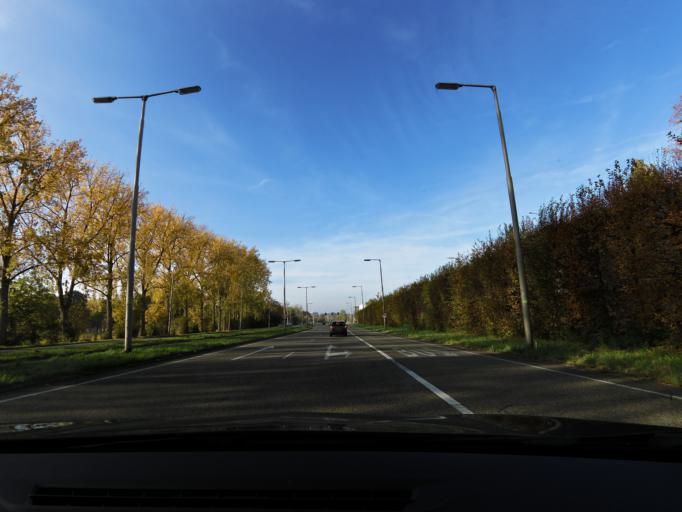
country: NL
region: South Holland
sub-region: Gemeente Ridderkerk
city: Ridderkerk
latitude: 51.8791
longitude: 4.5953
